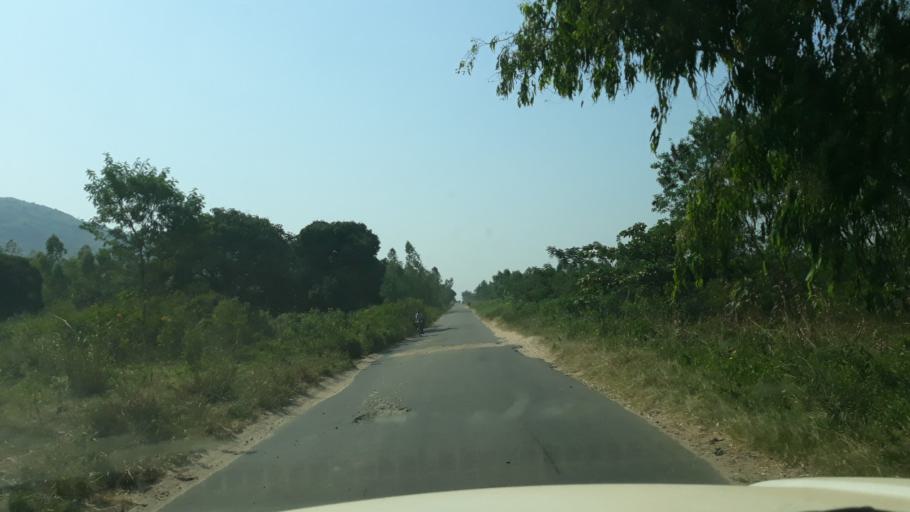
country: CD
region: South Kivu
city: Uvira
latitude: -3.3070
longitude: 29.1599
